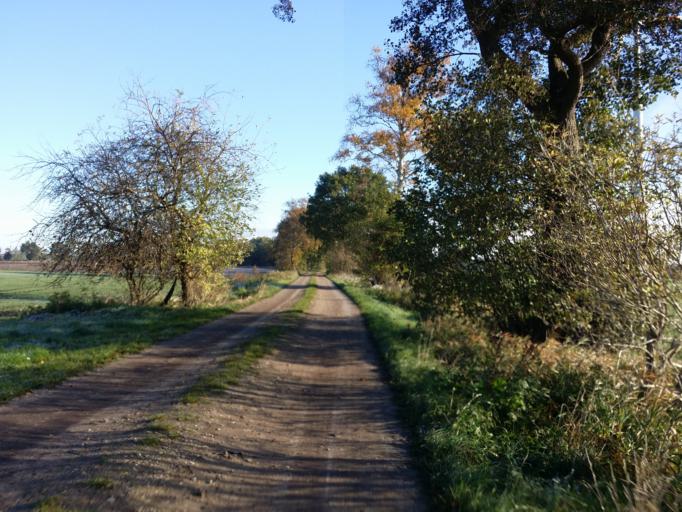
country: DE
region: Lower Saxony
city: Tarmstedt
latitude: 53.1970
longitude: 9.0517
